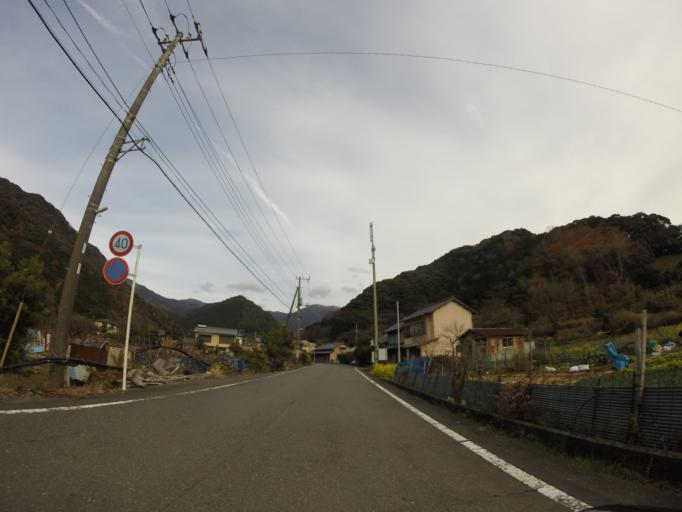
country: JP
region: Shizuoka
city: Heda
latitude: 34.8489
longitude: 138.7936
